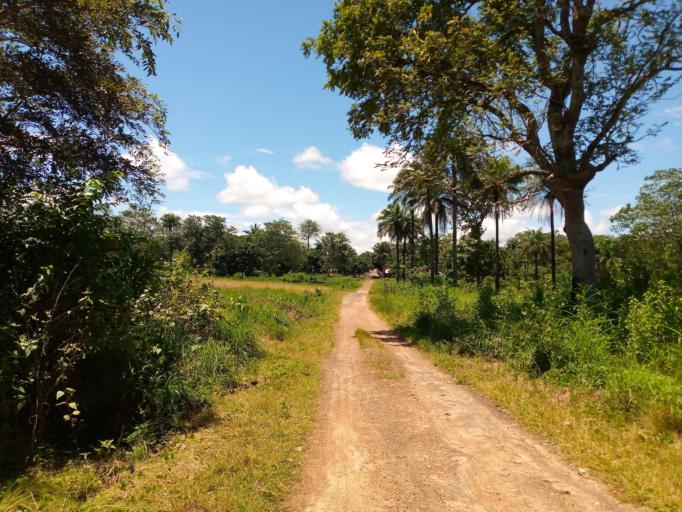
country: SL
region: Northern Province
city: Binkolo
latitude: 9.1021
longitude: -12.1414
